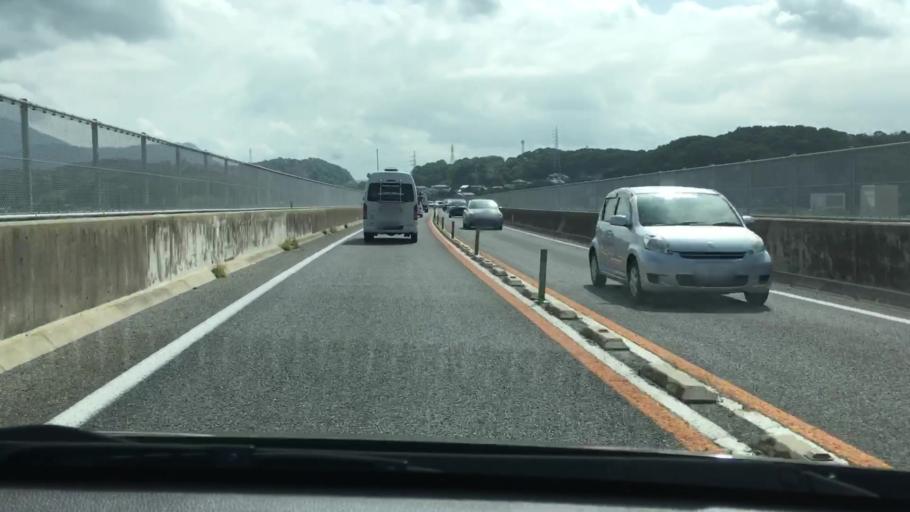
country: JP
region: Nagasaki
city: Sasebo
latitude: 33.1508
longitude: 129.7459
